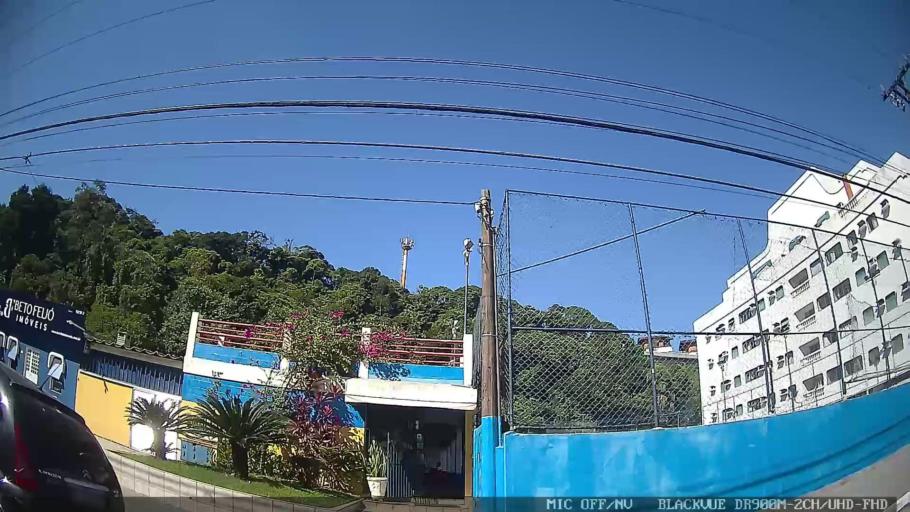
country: BR
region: Sao Paulo
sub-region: Guaruja
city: Guaruja
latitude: -23.9866
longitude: -46.2405
